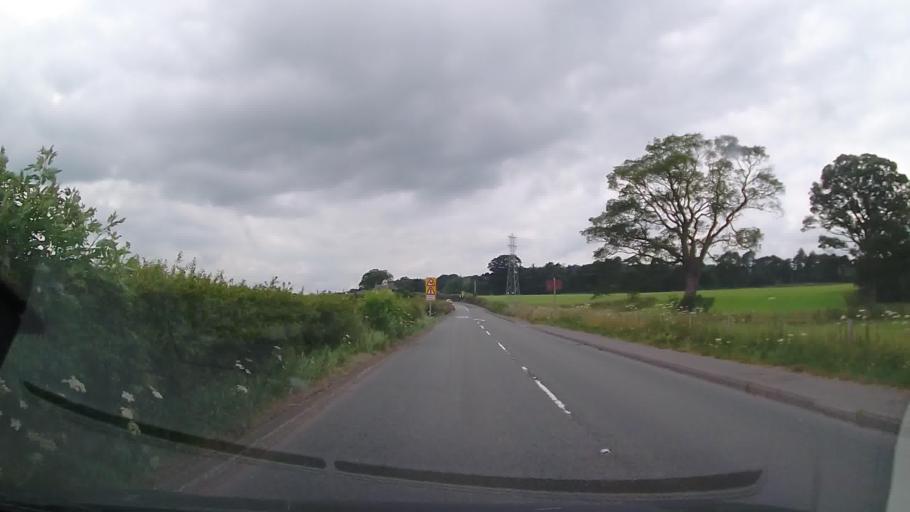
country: GB
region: Wales
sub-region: Denbighshire
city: Corwen
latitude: 52.9813
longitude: -3.3922
